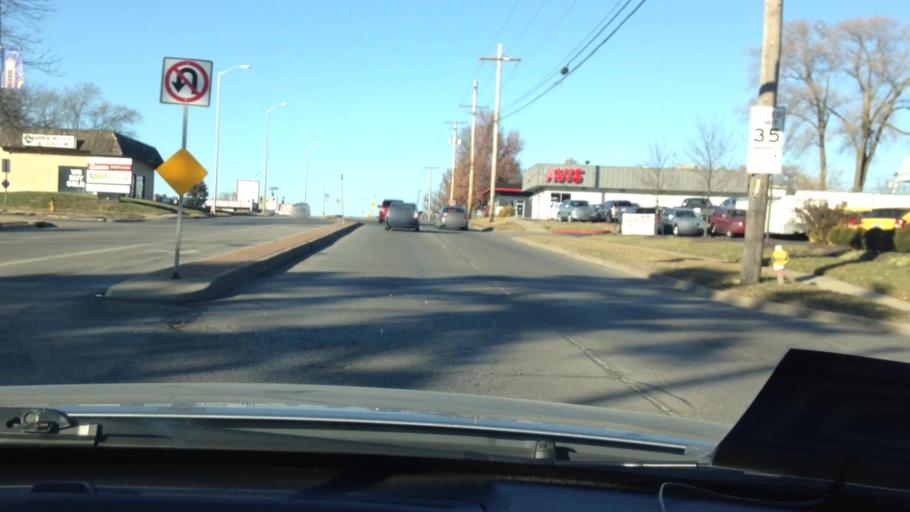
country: US
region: Kansas
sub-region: Johnson County
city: Overland Park
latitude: 38.9733
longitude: -94.6676
